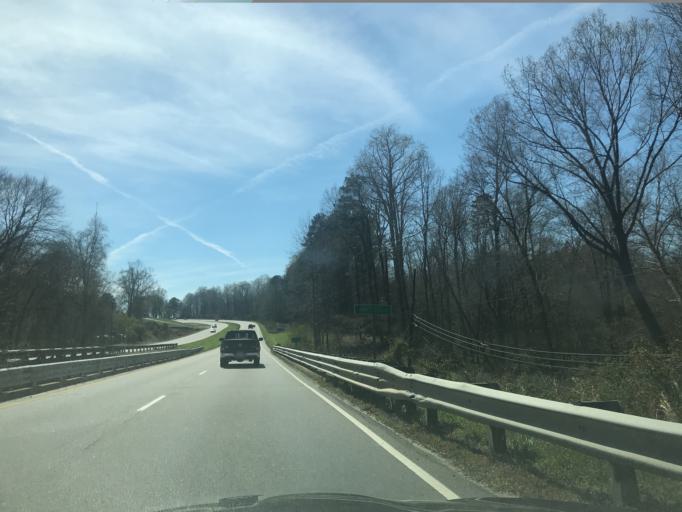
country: US
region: North Carolina
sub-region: Wake County
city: Garner
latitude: 35.6878
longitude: -78.6806
